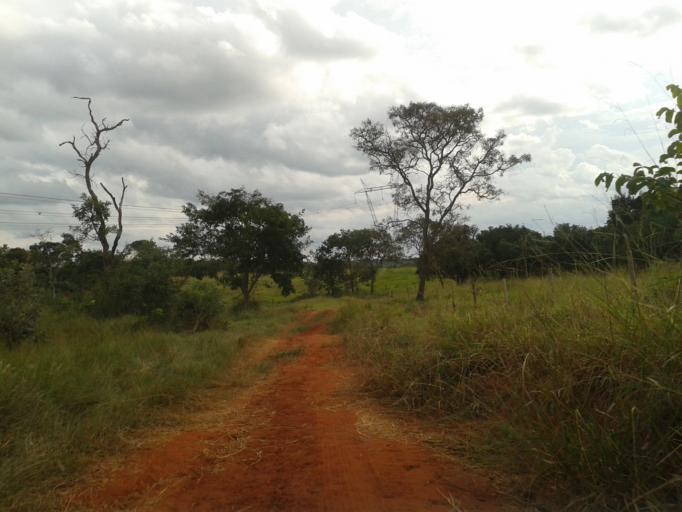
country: BR
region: Minas Gerais
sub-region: Campina Verde
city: Campina Verde
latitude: -19.4398
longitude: -49.5935
